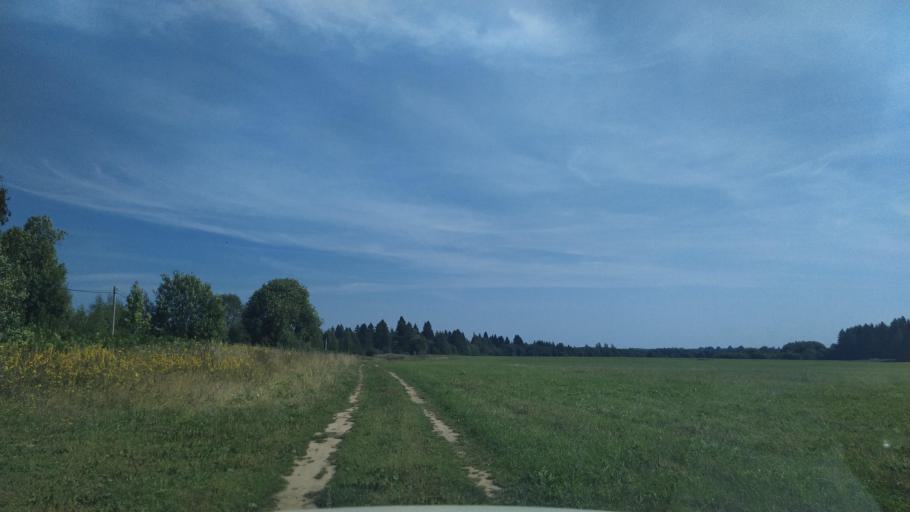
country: RU
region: Leningrad
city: Druzhnaya Gorka
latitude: 59.2686
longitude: 30.0565
